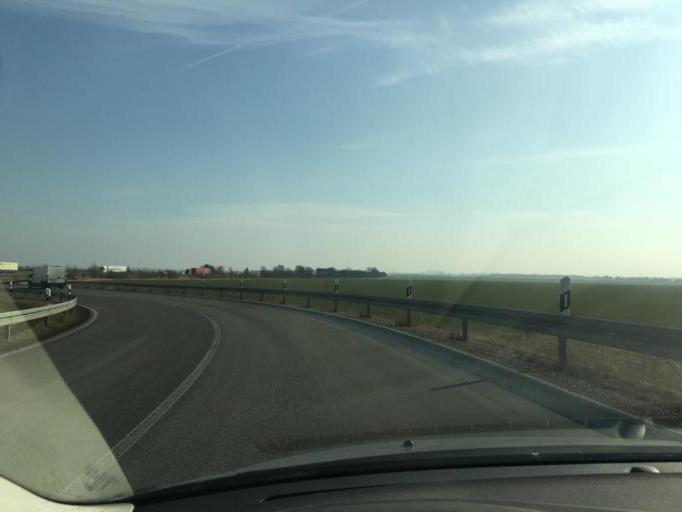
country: DE
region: Saxony-Anhalt
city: Grosskugel
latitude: 51.4389
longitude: 12.1427
